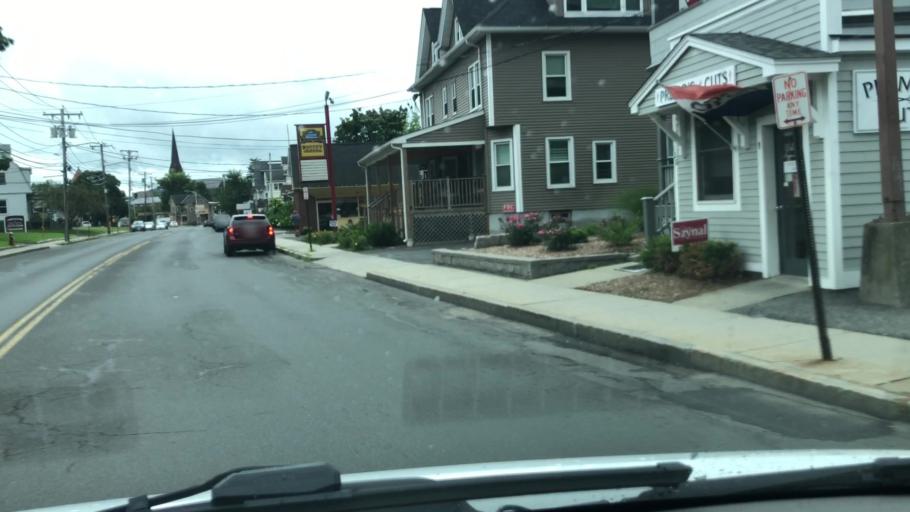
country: US
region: Massachusetts
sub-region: Hampshire County
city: Northampton
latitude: 42.3238
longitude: -72.6326
